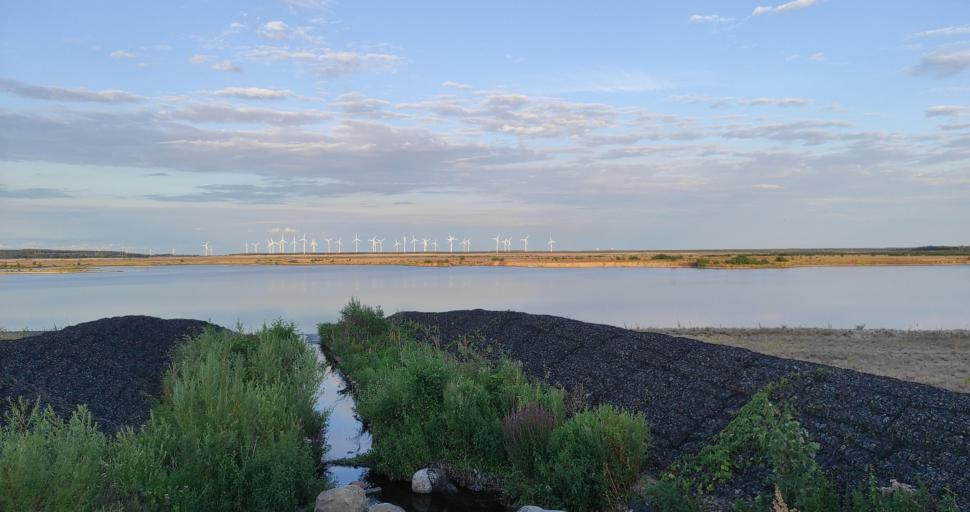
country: DE
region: Brandenburg
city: Cottbus
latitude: 51.7944
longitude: 14.3821
